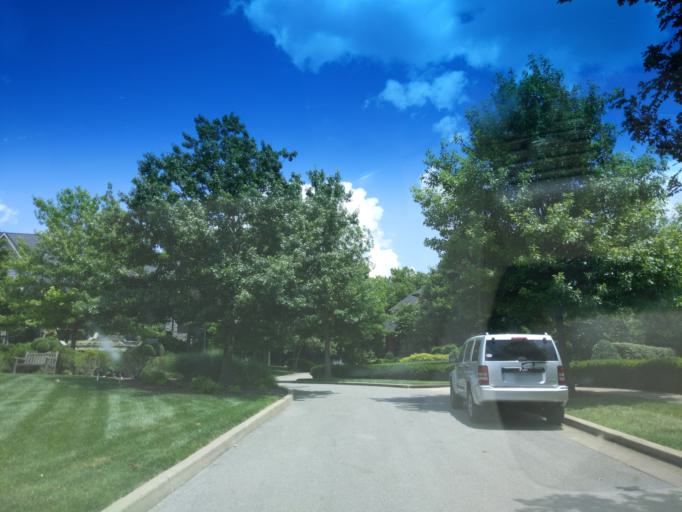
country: US
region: Tennessee
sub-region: Williamson County
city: Brentwood Estates
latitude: 36.0260
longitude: -86.7676
